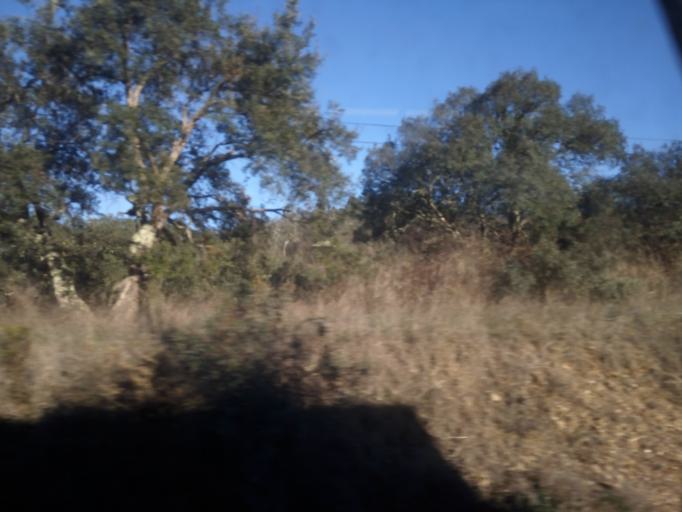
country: PT
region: Beja
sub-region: Odemira
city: Odemira
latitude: 37.5269
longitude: -8.4751
